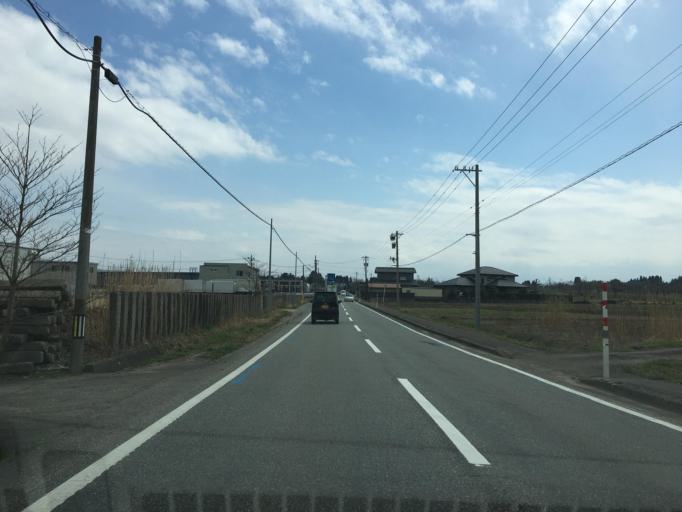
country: JP
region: Toyama
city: Kuragaki-kosugi
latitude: 36.6779
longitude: 137.1243
